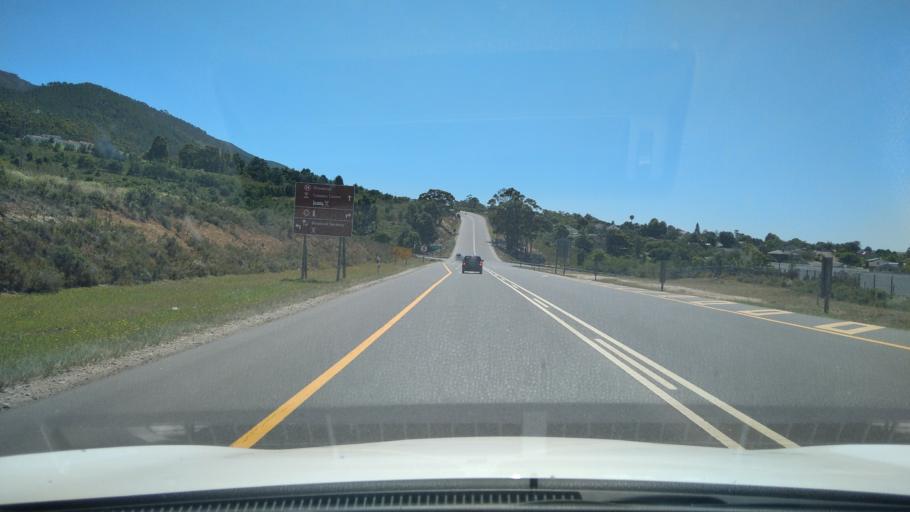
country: ZA
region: Western Cape
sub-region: Overberg District Municipality
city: Caledon
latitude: -34.2277
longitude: 19.4268
